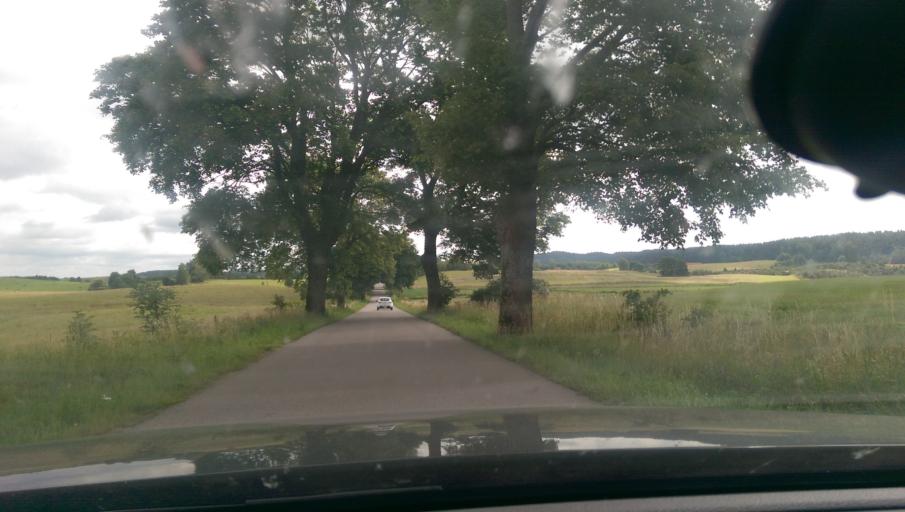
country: PL
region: Warmian-Masurian Voivodeship
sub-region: Powiat wegorzewski
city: Pozezdrze
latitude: 54.1928
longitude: 21.9237
